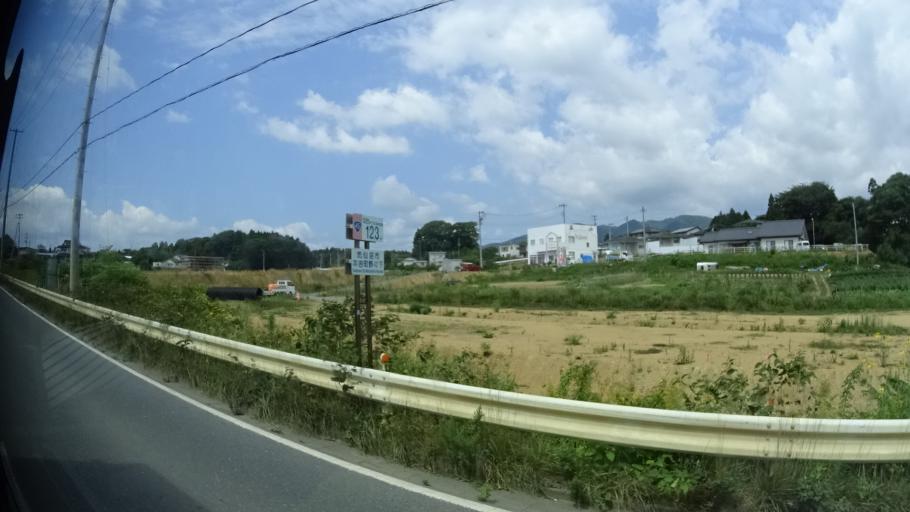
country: JP
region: Iwate
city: Ofunato
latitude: 38.8231
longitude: 141.5741
